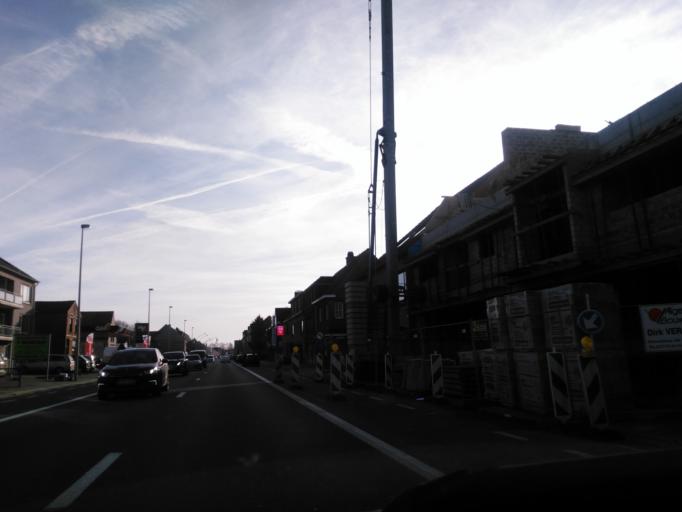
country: BE
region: Flanders
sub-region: Provincie Oost-Vlaanderen
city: Stekene
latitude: 51.2114
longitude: 4.0724
